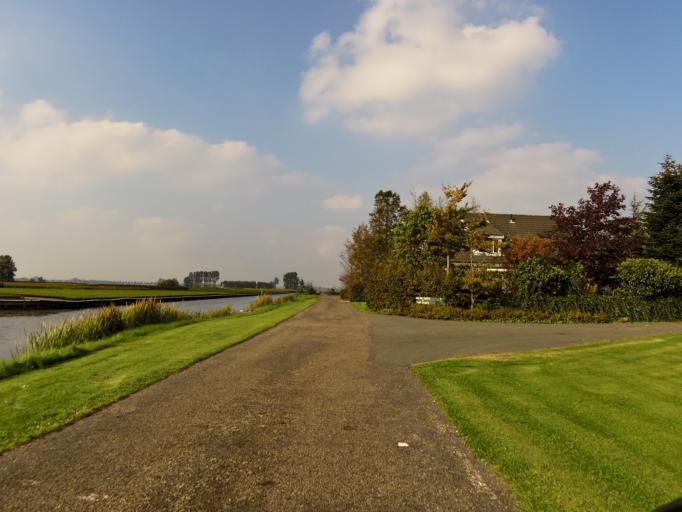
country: NL
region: South Holland
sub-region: Gemeente Rijnwoude
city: Benthuizen
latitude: 52.1067
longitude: 4.5478
